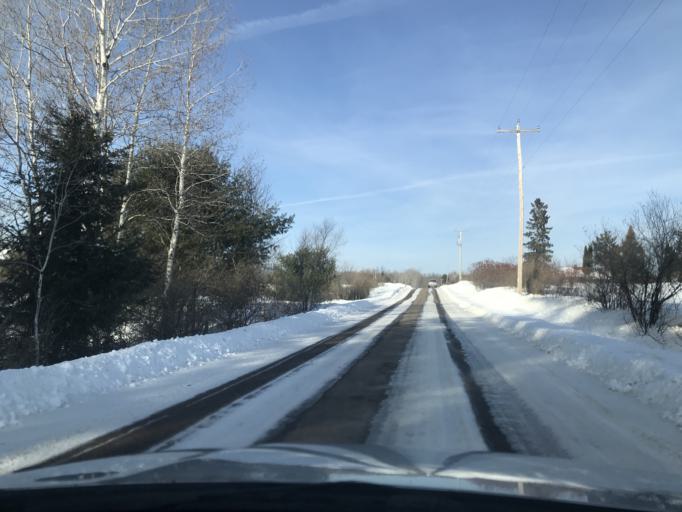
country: US
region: Wisconsin
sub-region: Menominee County
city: Legend Lake
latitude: 45.3128
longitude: -88.5217
